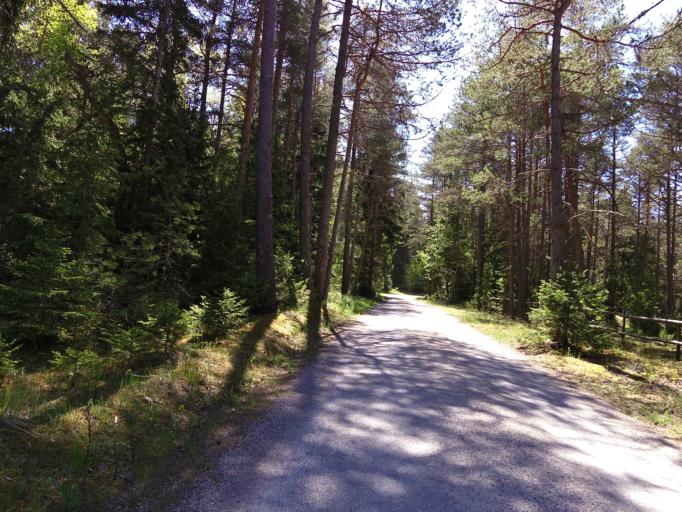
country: EE
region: Harju
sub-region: Paldiski linn
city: Paldiski
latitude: 59.2707
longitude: 23.7776
